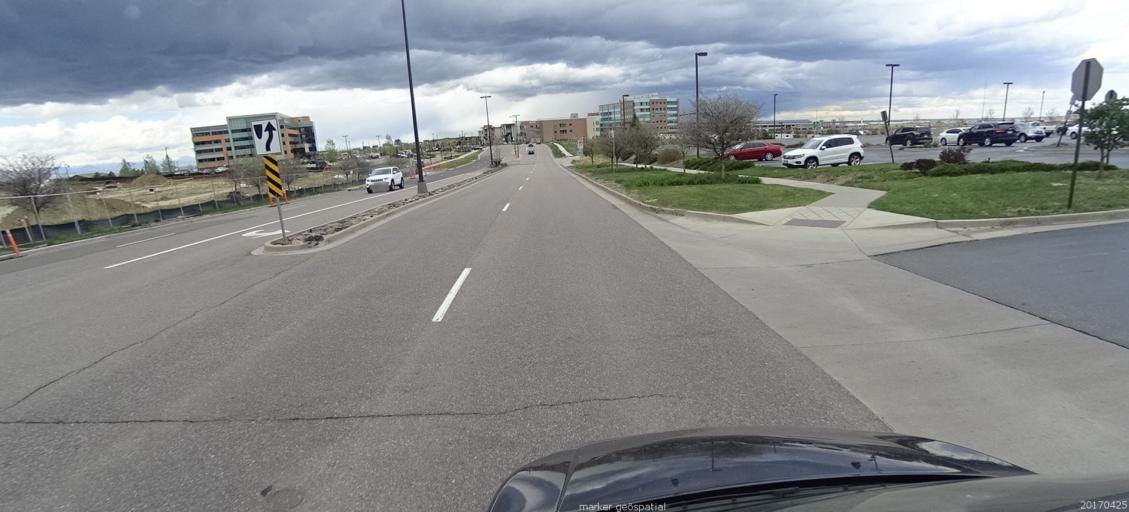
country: US
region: Colorado
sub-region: Douglas County
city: Meridian
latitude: 39.5418
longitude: -104.8709
